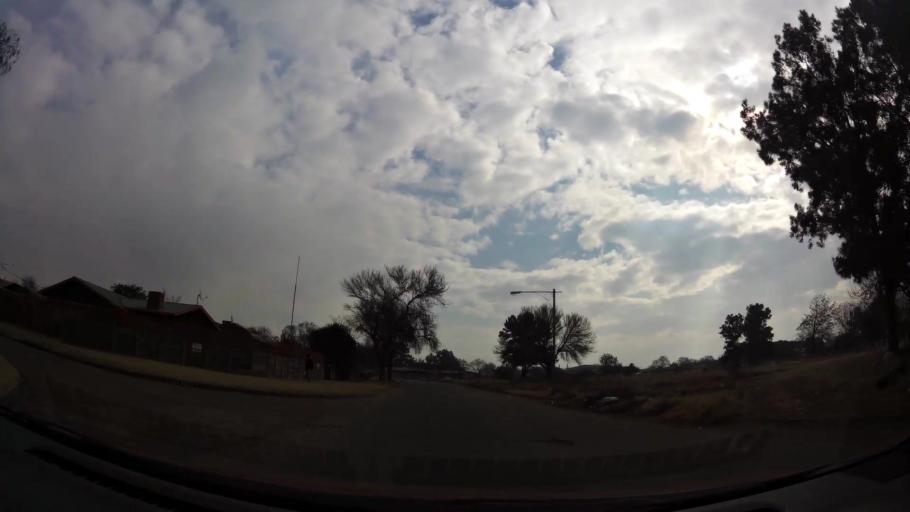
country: ZA
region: Gauteng
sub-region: Sedibeng District Municipality
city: Vanderbijlpark
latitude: -26.6825
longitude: 27.8329
